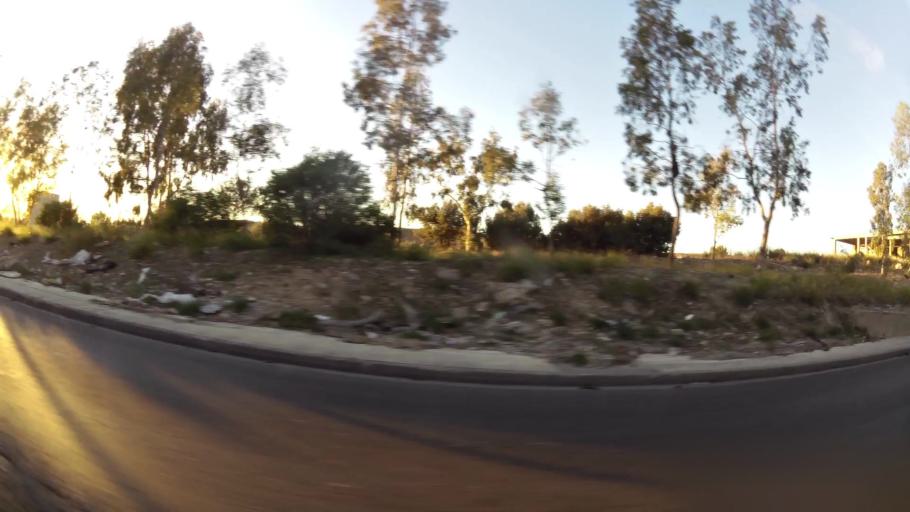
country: GR
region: Attica
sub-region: Nomarchia Athinas
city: Petroupolis
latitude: 38.0617
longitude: 23.6641
